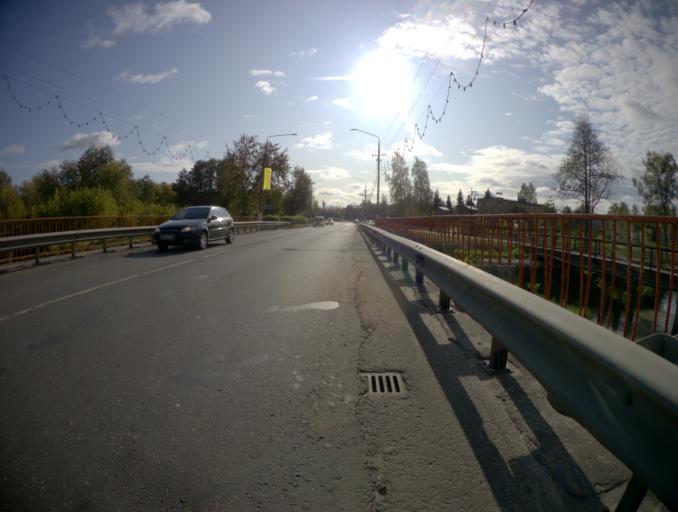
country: RU
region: Moskovskaya
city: Roshal'
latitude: 55.6631
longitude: 39.8660
